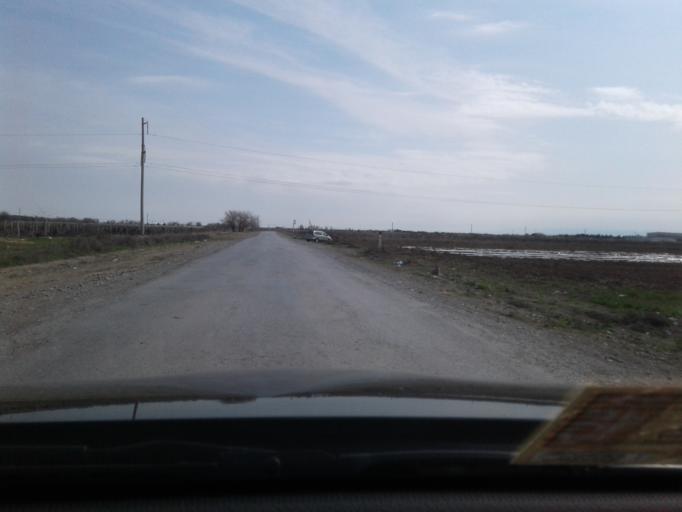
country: TM
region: Ahal
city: Ashgabat
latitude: 38.1177
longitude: 58.3566
